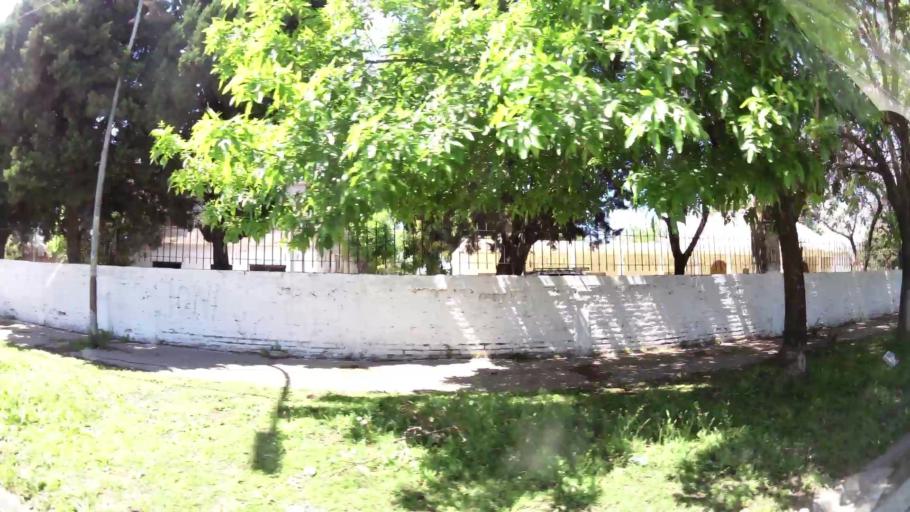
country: AR
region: Buenos Aires
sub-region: Partido de Lanus
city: Lanus
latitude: -34.6923
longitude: -58.4298
